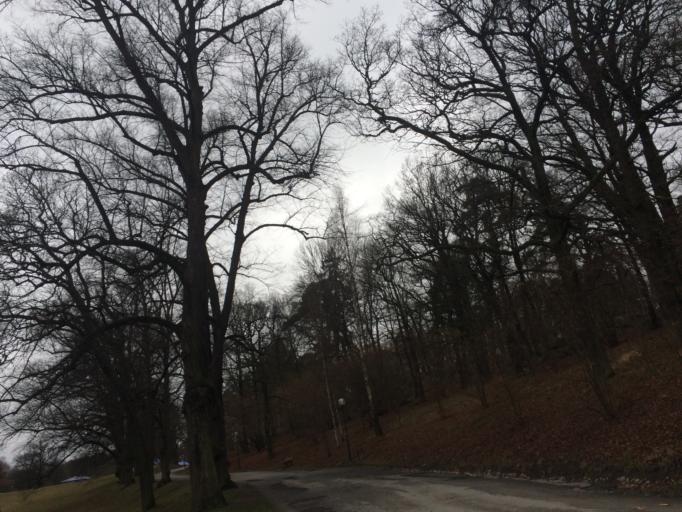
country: SE
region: Stockholm
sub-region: Norrtalje Kommun
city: Bergshamra
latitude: 59.3634
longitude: 18.0352
